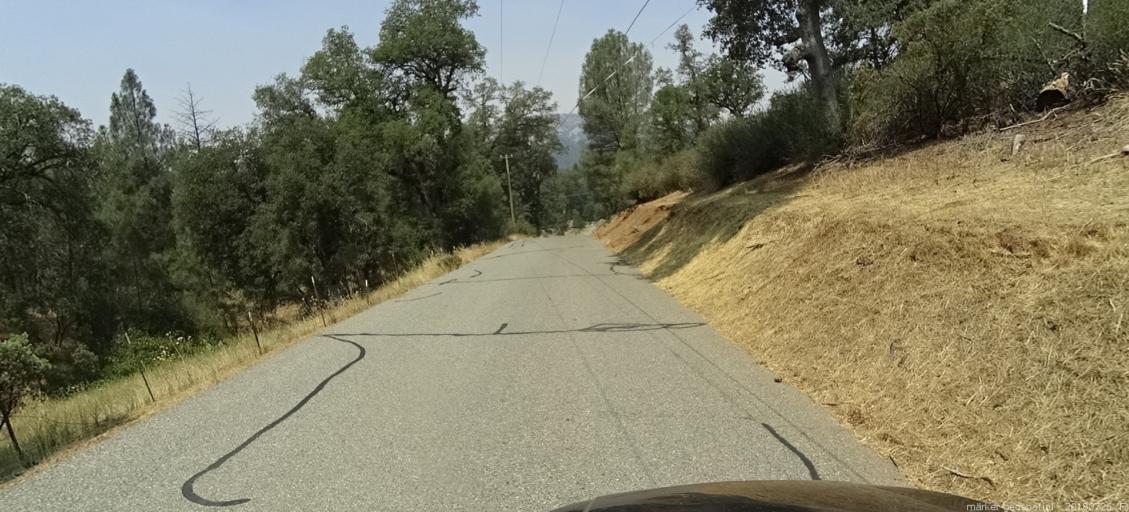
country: US
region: California
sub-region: Madera County
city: Oakhurst
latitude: 37.2844
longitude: -119.6522
